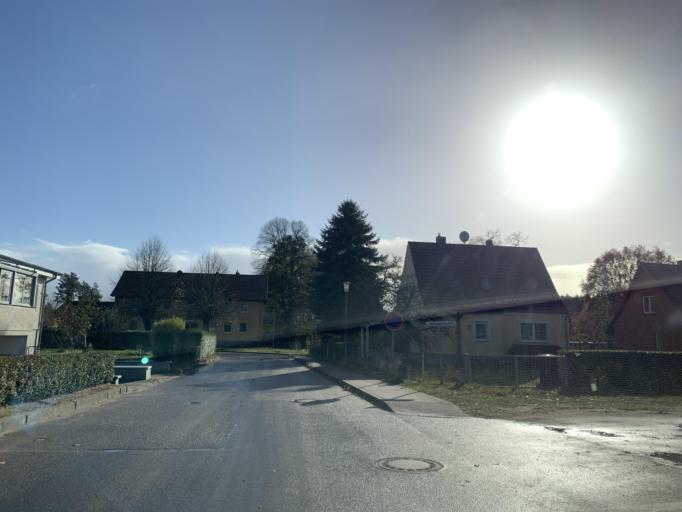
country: DE
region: Mecklenburg-Vorpommern
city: Blankensee
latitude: 53.4046
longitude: 13.2677
